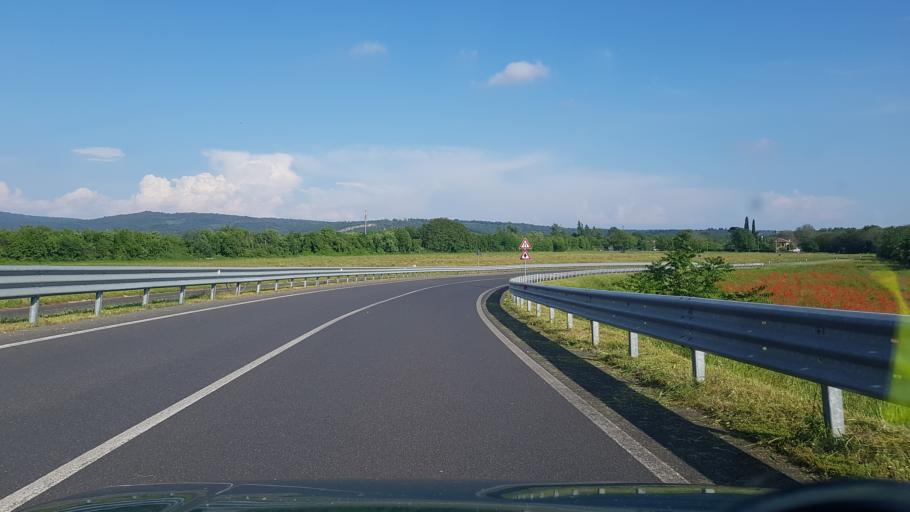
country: IT
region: Friuli Venezia Giulia
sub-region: Provincia di Gorizia
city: Sagrado
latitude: 45.8858
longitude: 13.4672
